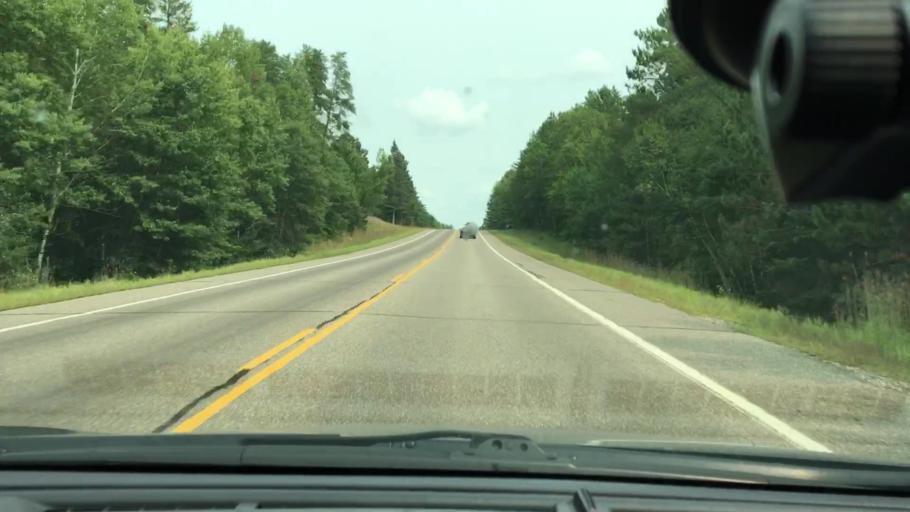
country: US
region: Minnesota
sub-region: Crow Wing County
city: Cross Lake
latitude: 46.7309
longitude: -93.9823
